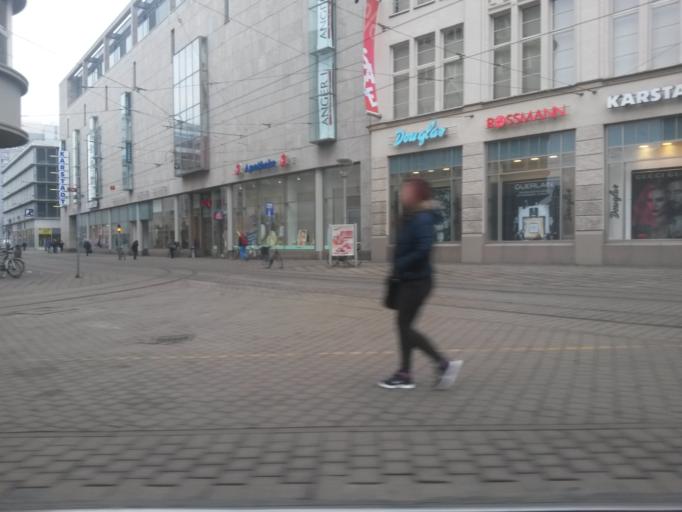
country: DE
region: Thuringia
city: Erfurt
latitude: 50.9778
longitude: 11.0357
